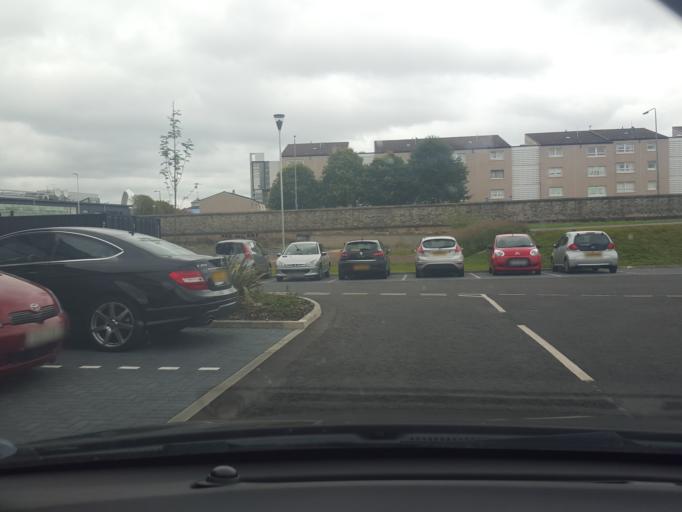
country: GB
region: Scotland
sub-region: Glasgow City
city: Glasgow
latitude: 55.8559
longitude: -4.2890
